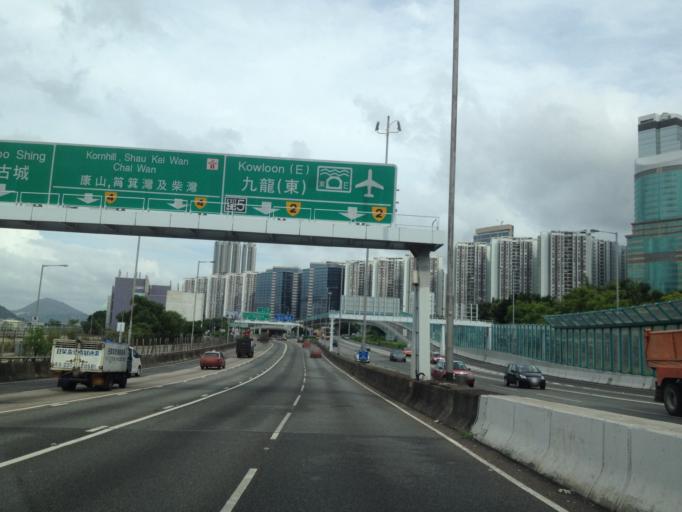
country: HK
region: Kowloon City
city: Kowloon
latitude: 22.2913
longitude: 114.2113
